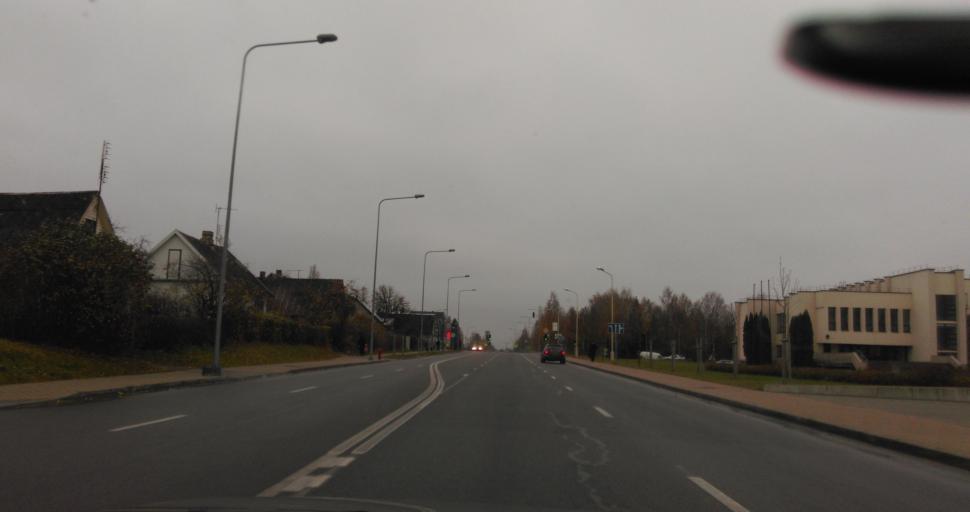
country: LT
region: Panevezys
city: Rokiskis
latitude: 55.9551
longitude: 25.5885
